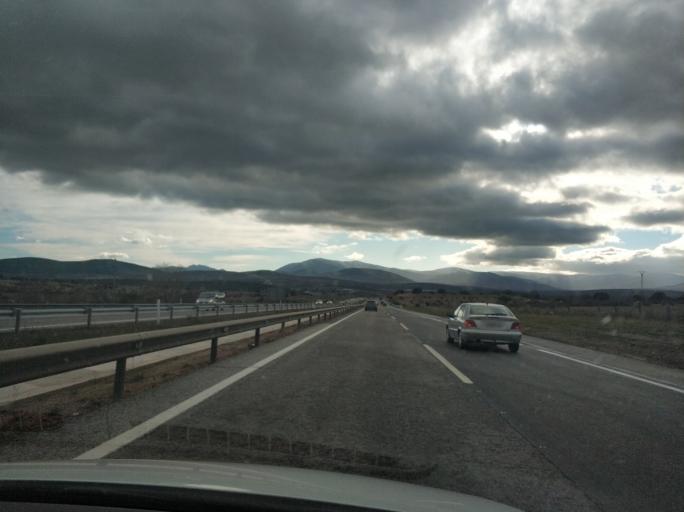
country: ES
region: Madrid
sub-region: Provincia de Madrid
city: Gascones
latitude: 41.0183
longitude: -3.6278
